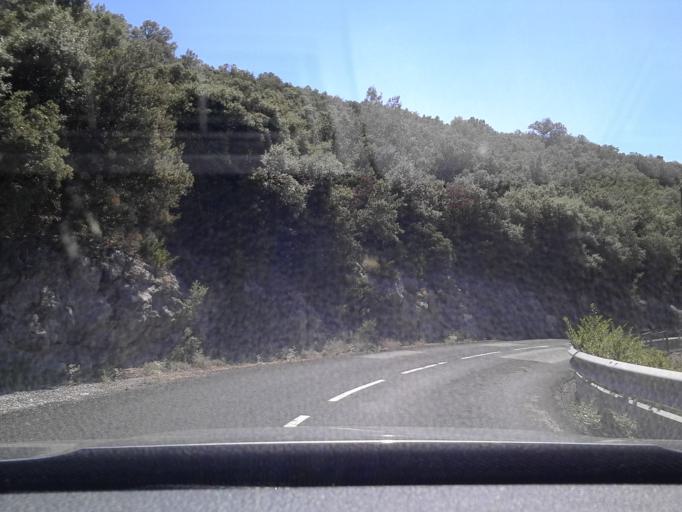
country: FR
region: Languedoc-Roussillon
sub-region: Departement de l'Herault
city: Montpeyroux
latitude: 43.7240
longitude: 3.4686
